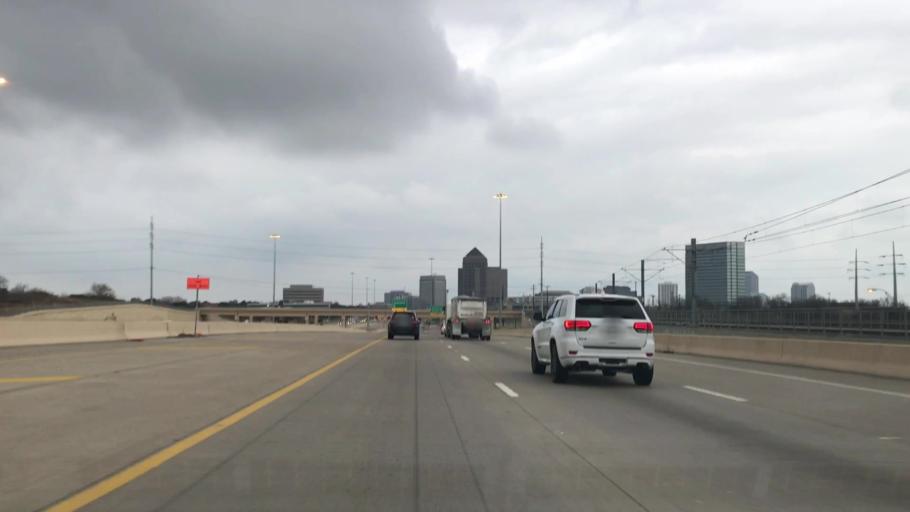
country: US
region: Texas
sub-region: Dallas County
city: Irving
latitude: 32.8530
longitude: -96.9232
